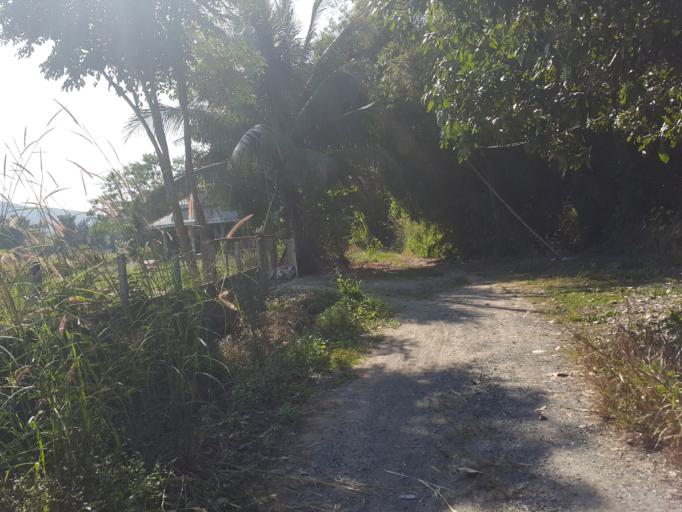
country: TH
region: Chiang Mai
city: Mae On
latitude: 18.7878
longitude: 99.1986
